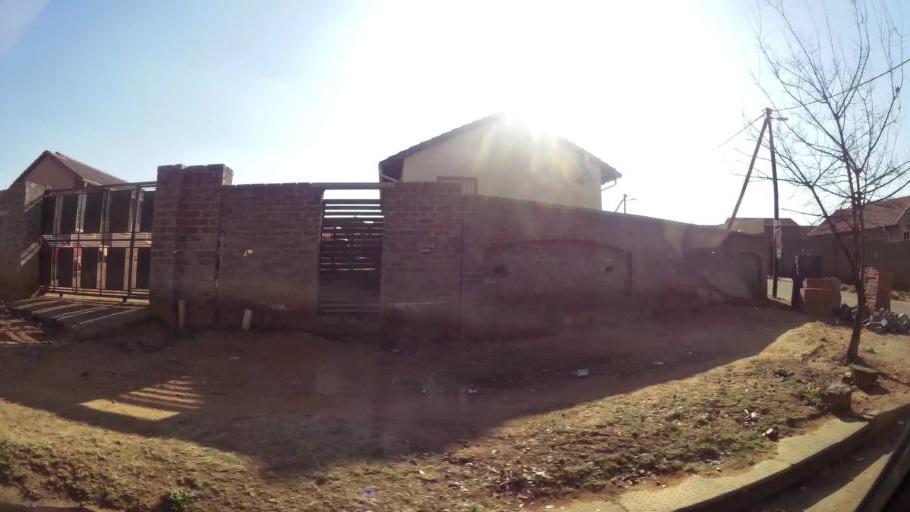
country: ZA
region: Gauteng
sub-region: West Rand District Municipality
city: Muldersdriseloop
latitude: -26.0339
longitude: 27.9184
